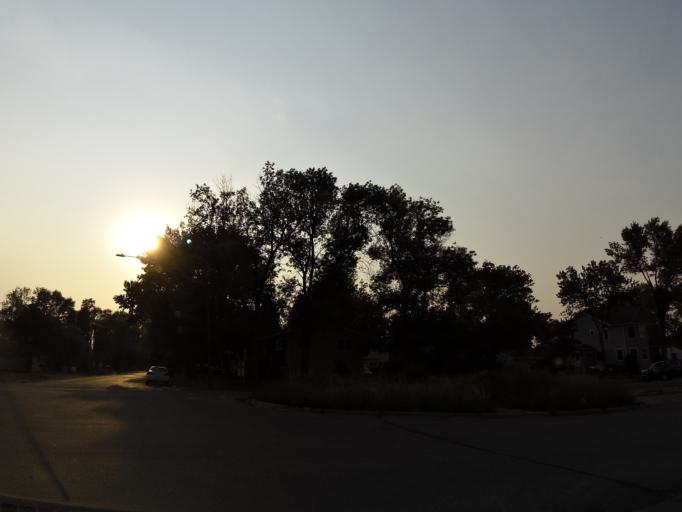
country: US
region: North Dakota
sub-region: Traill County
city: Mayville
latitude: 47.5001
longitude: -97.3173
